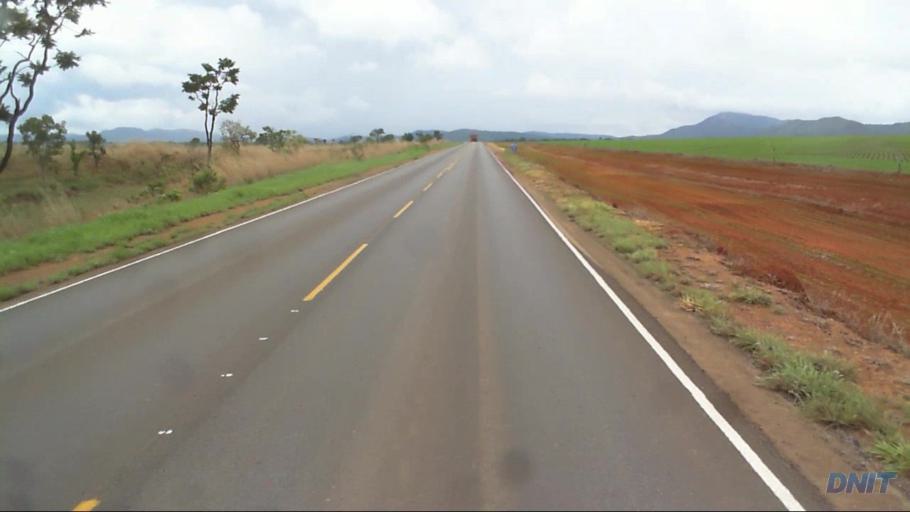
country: BR
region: Goias
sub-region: Padre Bernardo
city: Padre Bernardo
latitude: -15.3370
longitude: -48.2336
